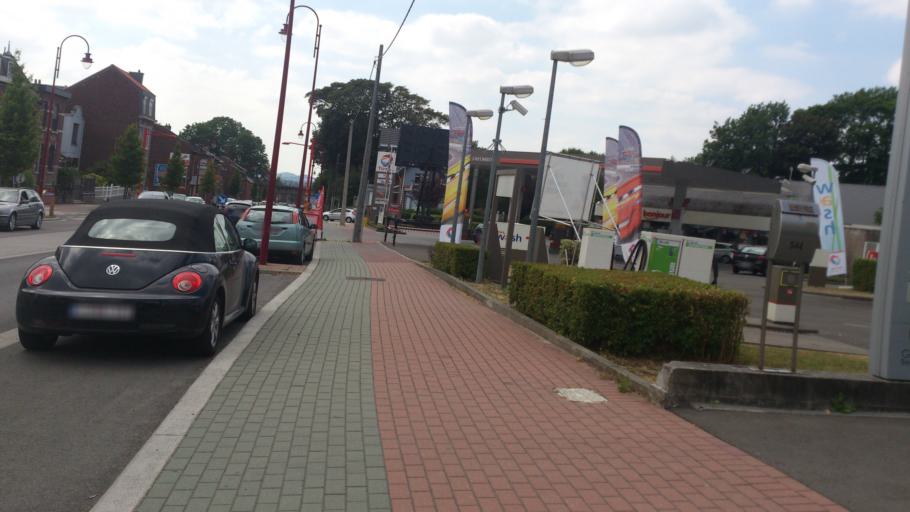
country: BE
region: Wallonia
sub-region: Province de Liege
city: Beyne-Heusay
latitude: 50.6263
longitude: 5.6395
